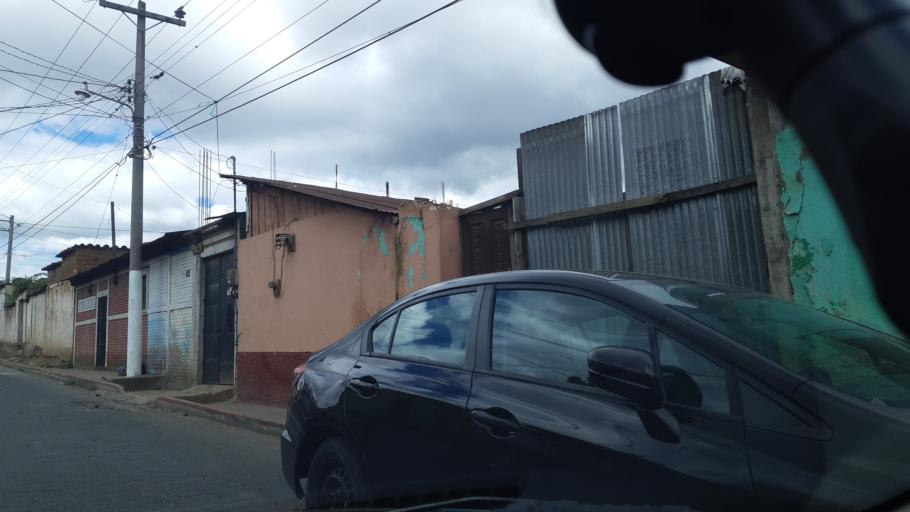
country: GT
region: Chimaltenango
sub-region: Municipio de Chimaltenango
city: Chimaltenango
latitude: 14.6630
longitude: -90.8237
